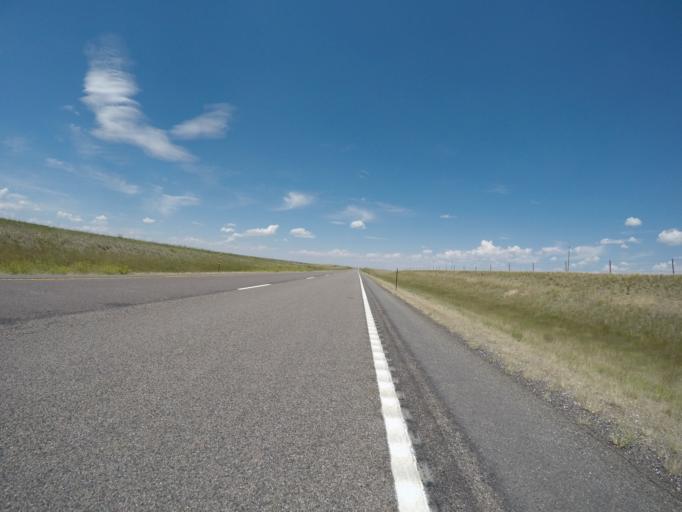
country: US
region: Wyoming
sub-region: Albany County
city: Laramie
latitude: 41.5940
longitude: -105.7120
